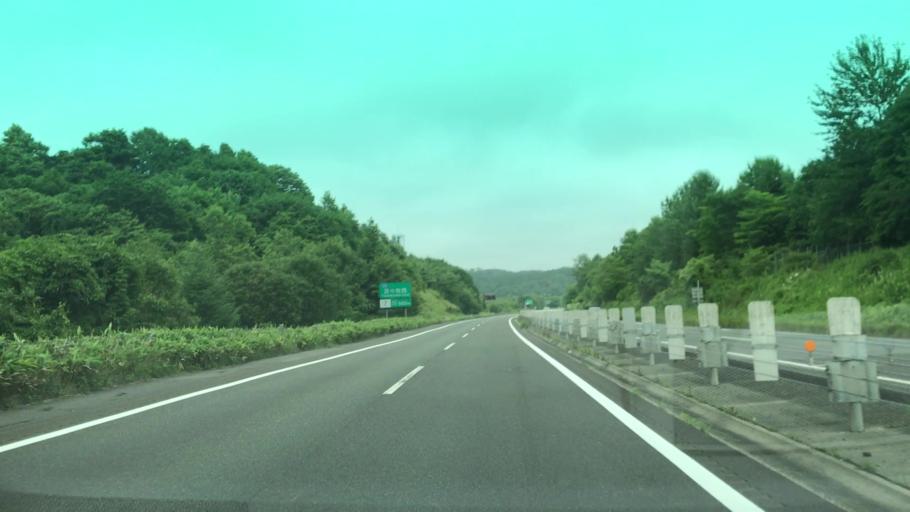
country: JP
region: Hokkaido
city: Tomakomai
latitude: 42.6270
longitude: 141.4831
